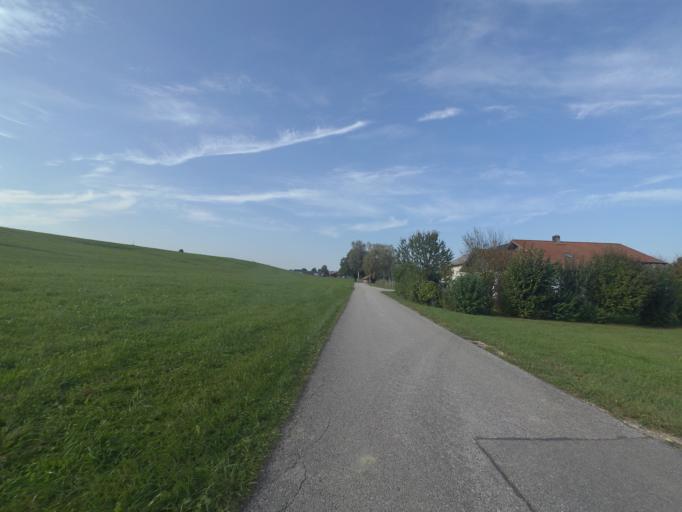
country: DE
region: Bavaria
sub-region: Upper Bavaria
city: Laufen
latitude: 47.9145
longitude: 12.8955
